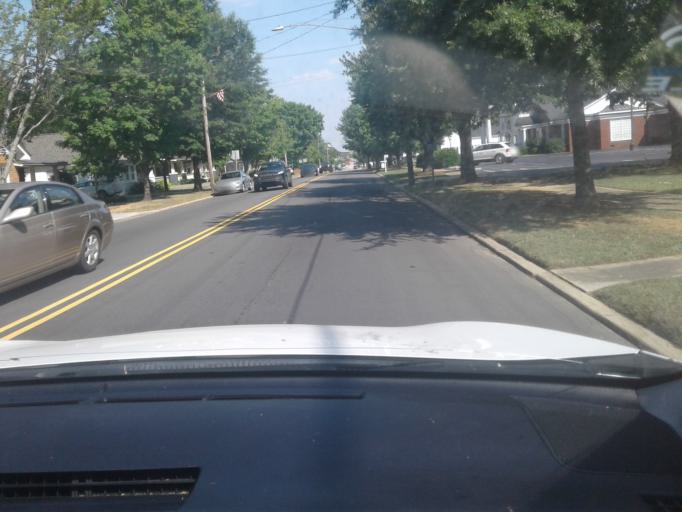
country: US
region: North Carolina
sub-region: Johnston County
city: Benson
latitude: 35.3836
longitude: -78.5518
